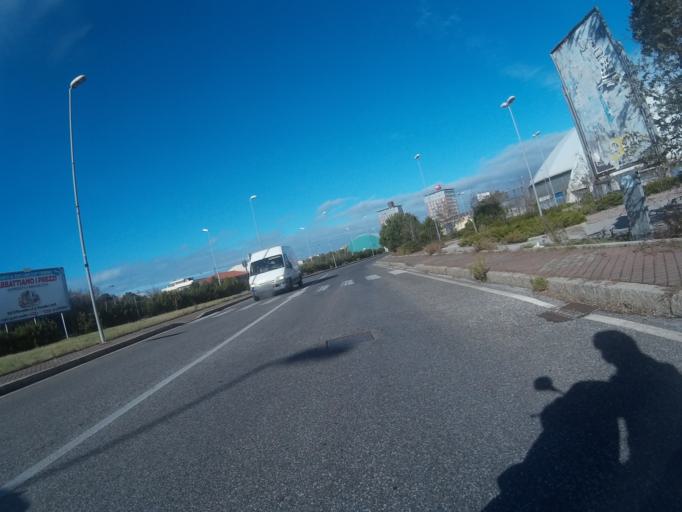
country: IT
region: Tuscany
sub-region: Provincia di Livorno
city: Livorno
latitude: 43.5538
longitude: 10.3419
